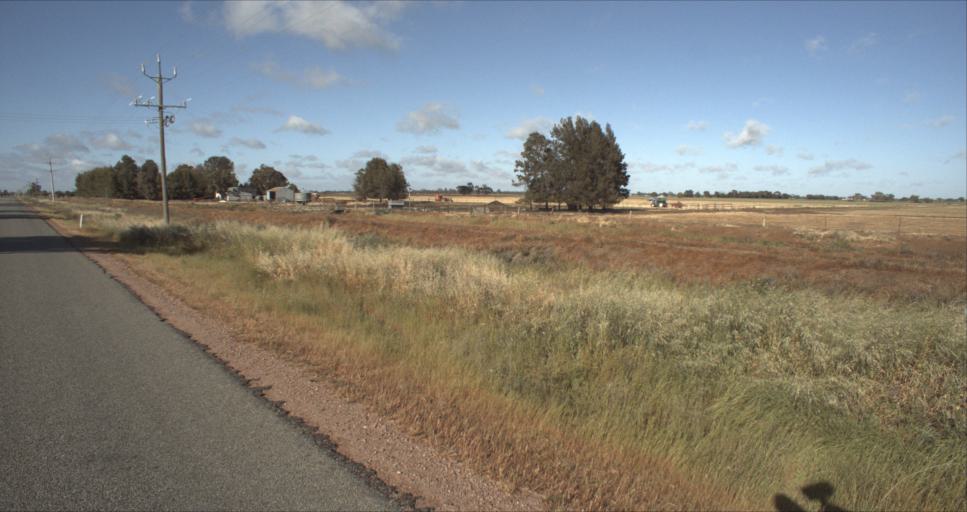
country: AU
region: New South Wales
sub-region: Leeton
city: Leeton
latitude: -34.5202
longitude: 146.3907
